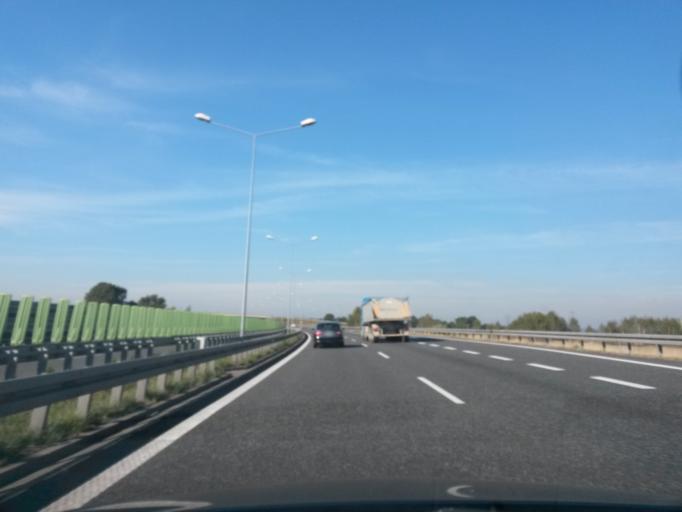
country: PL
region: Silesian Voivodeship
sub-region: Powiat gliwicki
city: Sosnicowice
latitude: 50.3423
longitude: 18.5432
